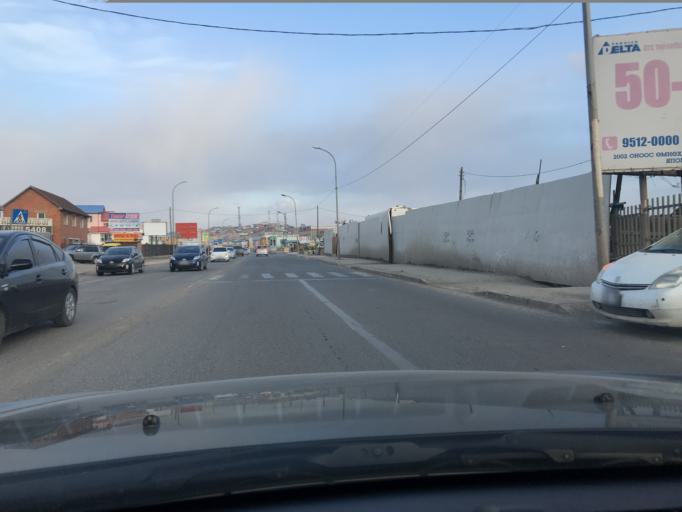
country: MN
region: Ulaanbaatar
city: Ulaanbaatar
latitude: 47.9243
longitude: 106.9894
